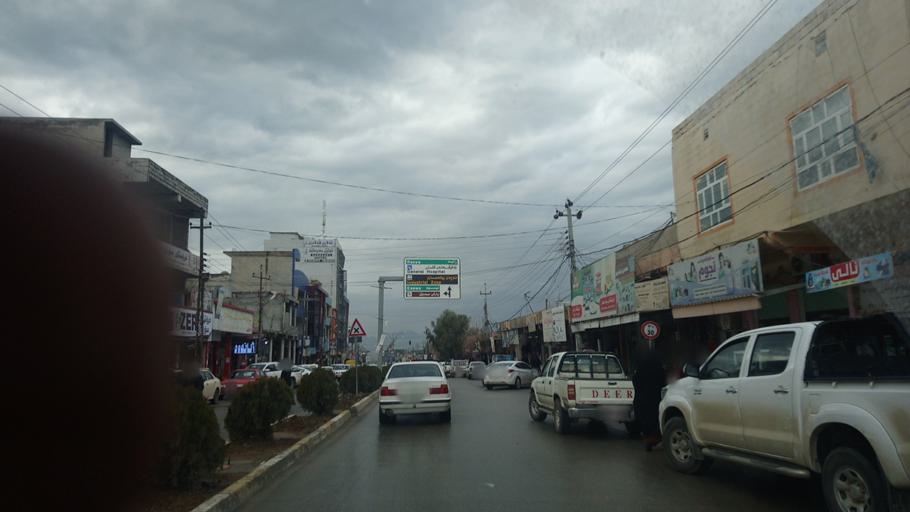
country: IQ
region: As Sulaymaniyah
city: Qeladize
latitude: 36.1810
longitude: 45.1302
